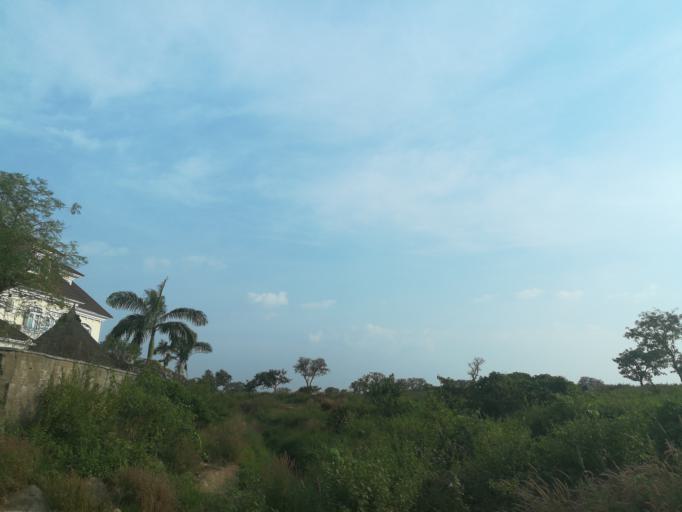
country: NG
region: Abuja Federal Capital Territory
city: Abuja
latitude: 9.0910
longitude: 7.3747
